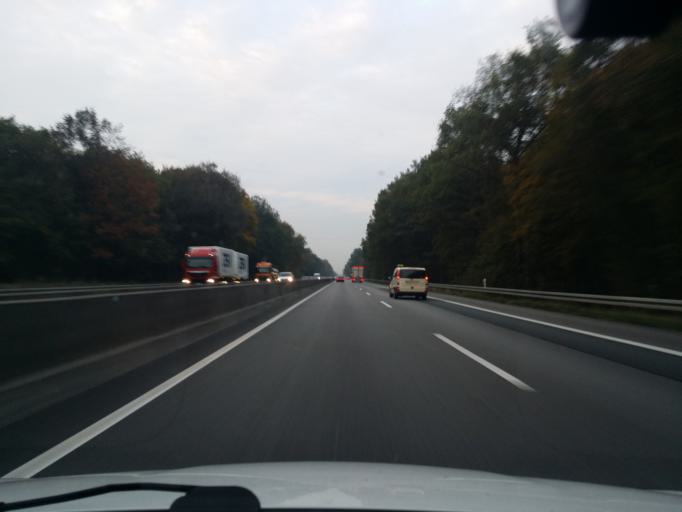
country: DE
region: Hesse
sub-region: Regierungsbezirk Darmstadt
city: Einhausen
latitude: 49.6838
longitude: 8.5527
